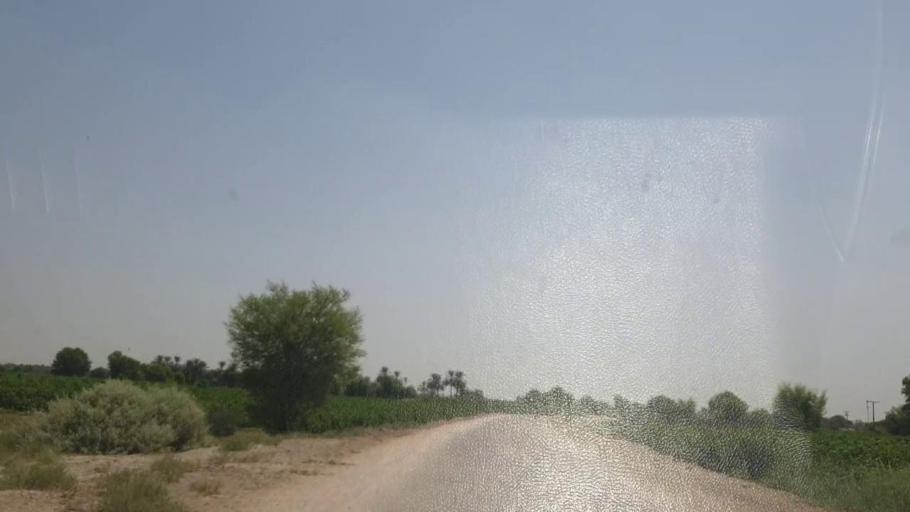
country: PK
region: Sindh
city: Bozdar
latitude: 27.2476
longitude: 68.6675
